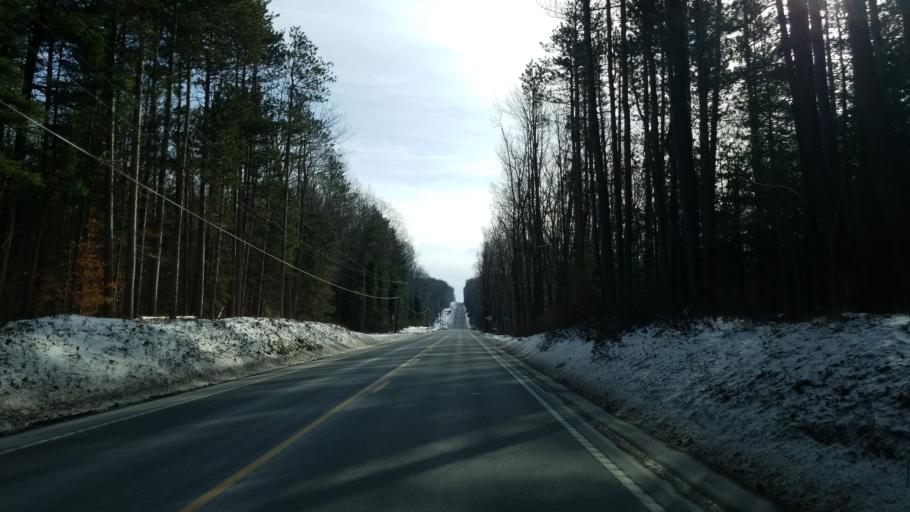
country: US
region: Pennsylvania
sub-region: Clearfield County
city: Clearfield
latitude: 41.1418
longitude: -78.5430
